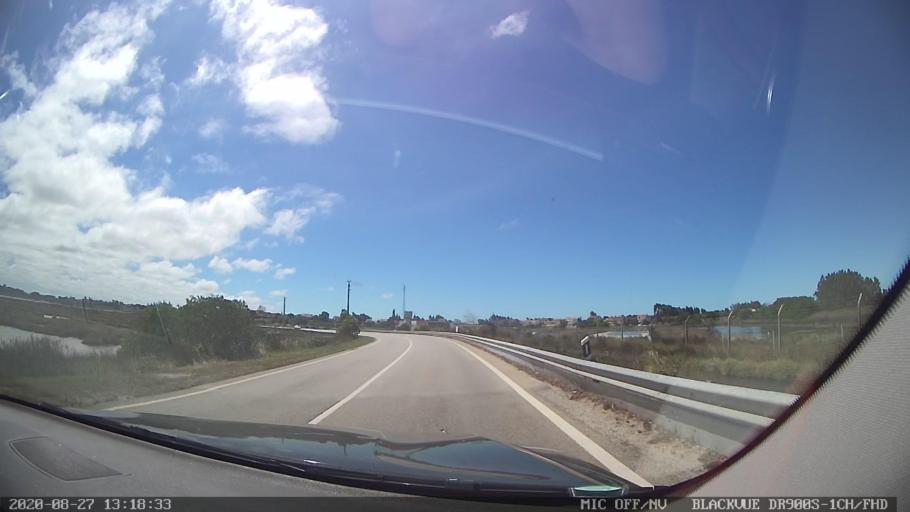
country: PT
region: Aveiro
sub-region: Vagos
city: Vagos
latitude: 40.5735
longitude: -8.6810
